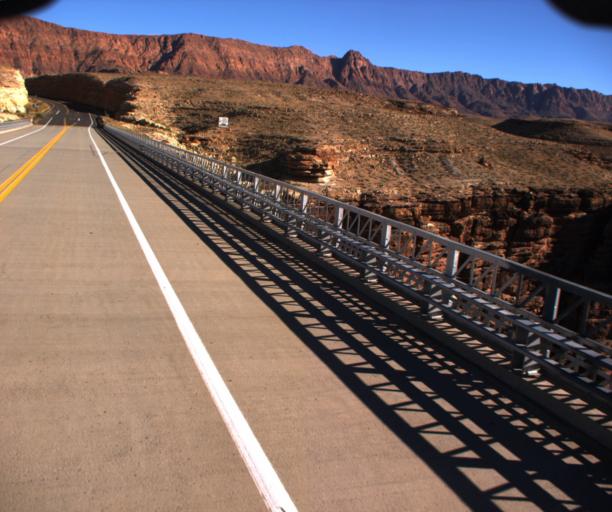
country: US
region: Arizona
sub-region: Coconino County
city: Page
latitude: 36.8172
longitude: -111.6316
